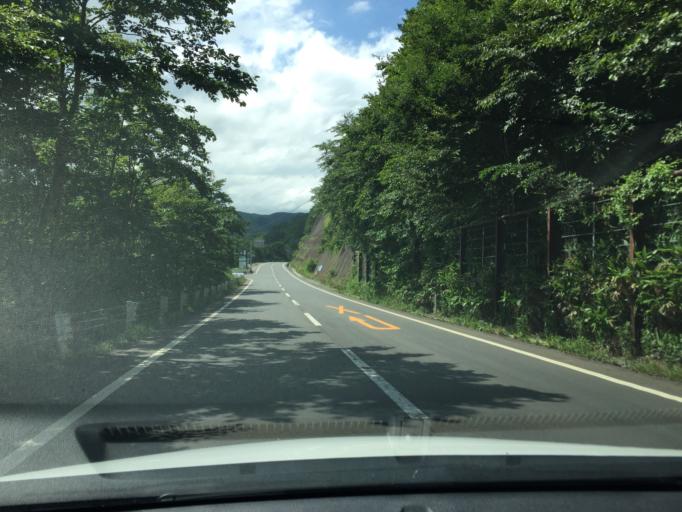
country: JP
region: Fukushima
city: Inawashiro
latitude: 37.2716
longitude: 140.0777
